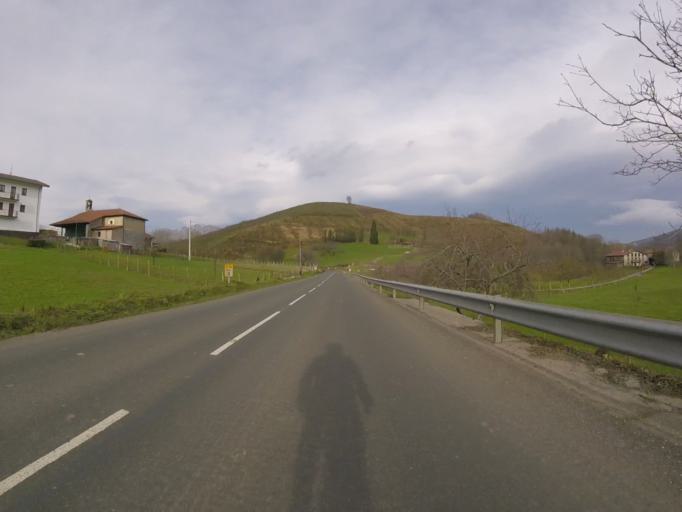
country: ES
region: Basque Country
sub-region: Provincia de Guipuzcoa
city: Azpeitia
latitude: 43.1680
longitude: -2.2304
